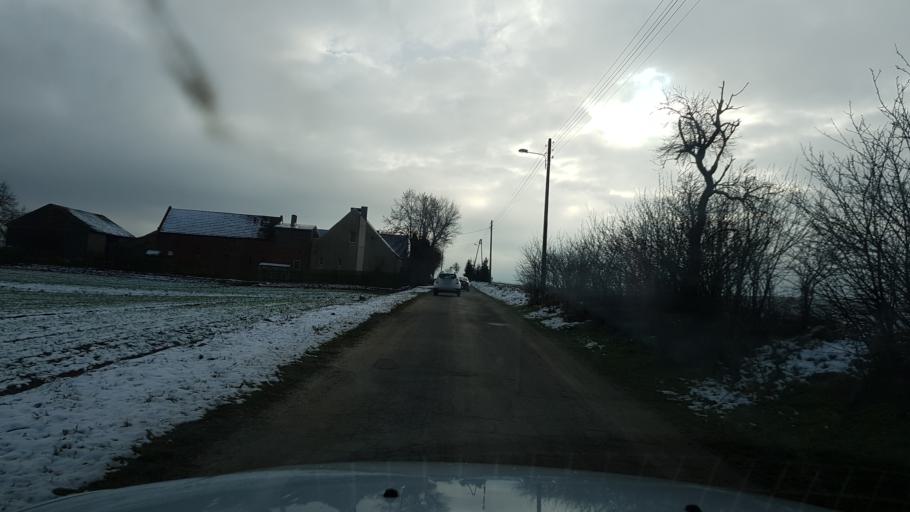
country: PL
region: West Pomeranian Voivodeship
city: Trzcinsko Zdroj
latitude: 52.9624
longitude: 14.6747
